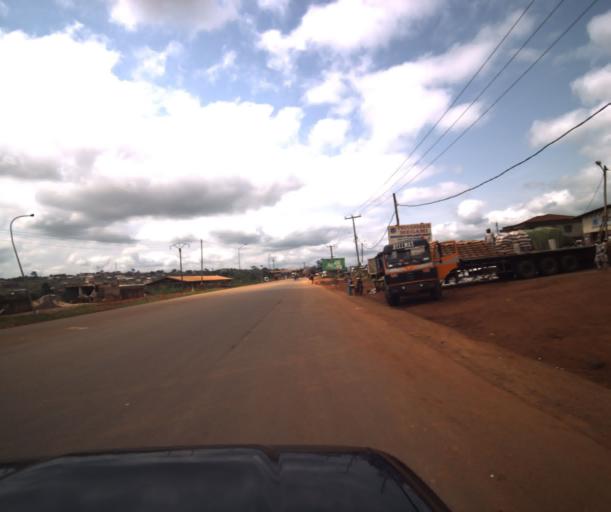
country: CM
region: Centre
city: Yaounde
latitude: 3.8079
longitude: 11.5100
